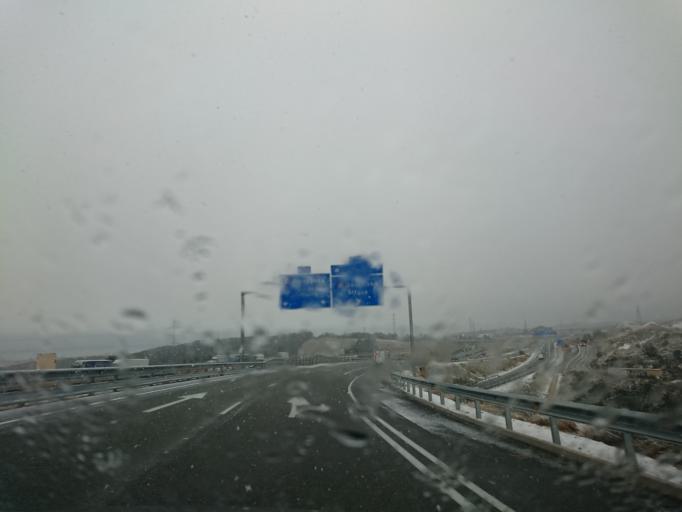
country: ES
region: Catalonia
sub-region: Provincia de Barcelona
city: Vilanova i la Geltru
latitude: 41.2581
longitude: 1.7316
